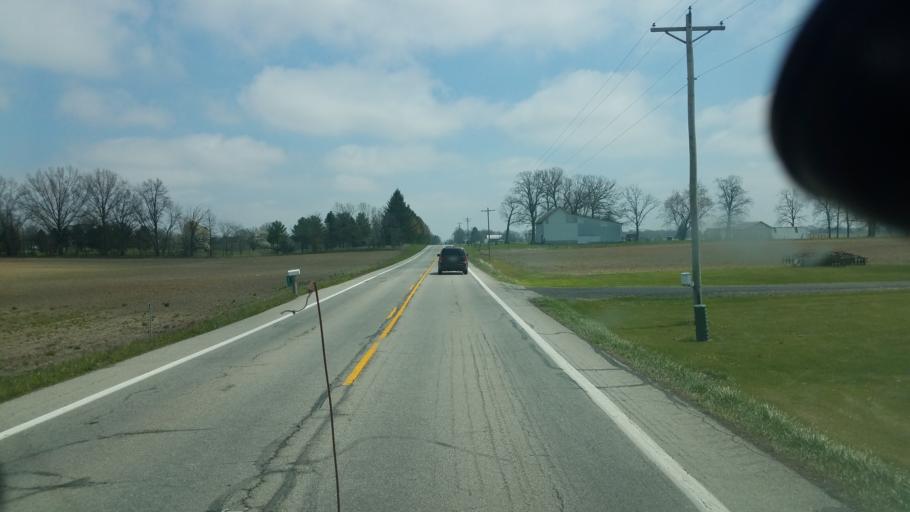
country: US
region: Ohio
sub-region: Morrow County
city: Cardington
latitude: 40.5842
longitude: -82.9845
